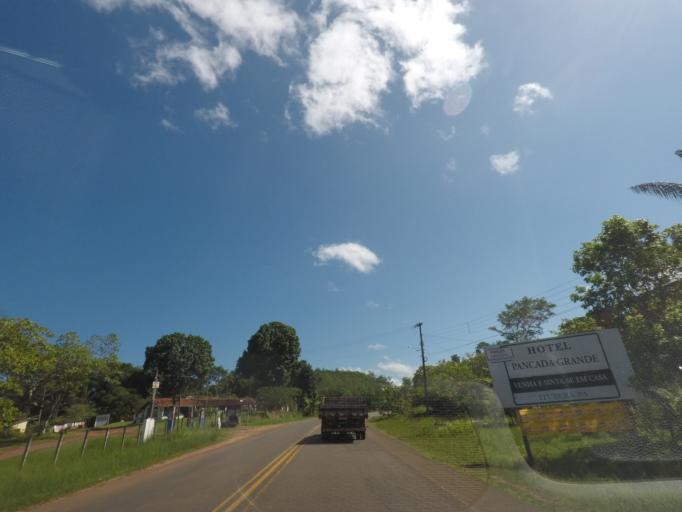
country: BR
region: Bahia
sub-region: Itubera
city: Itubera
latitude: -13.6954
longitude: -39.1330
